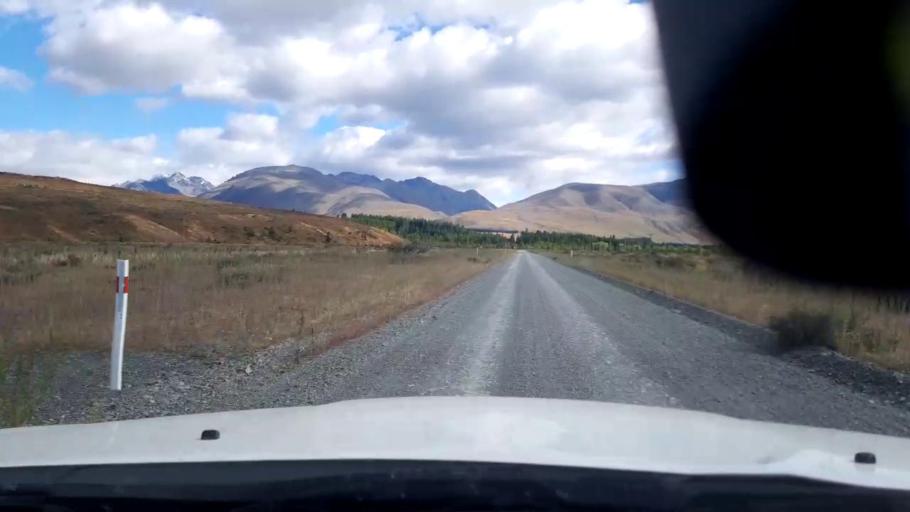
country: NZ
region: Canterbury
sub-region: Timaru District
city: Pleasant Point
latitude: -43.8836
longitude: 170.4668
